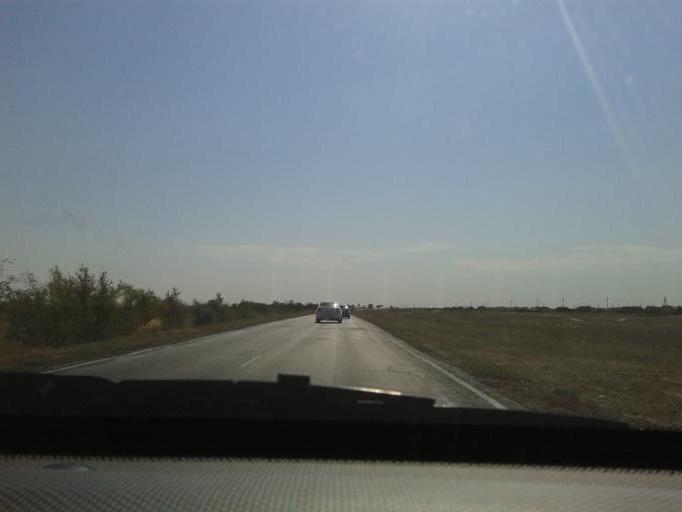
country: RU
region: Astrakhan
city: Znamensk
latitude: 48.5981
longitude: 45.6179
